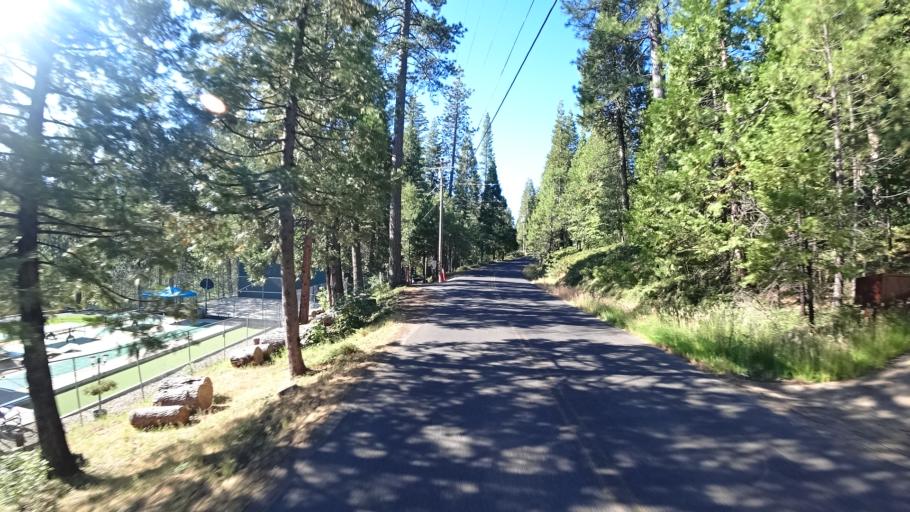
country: US
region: California
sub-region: Calaveras County
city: Arnold
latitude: 38.2620
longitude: -120.3315
